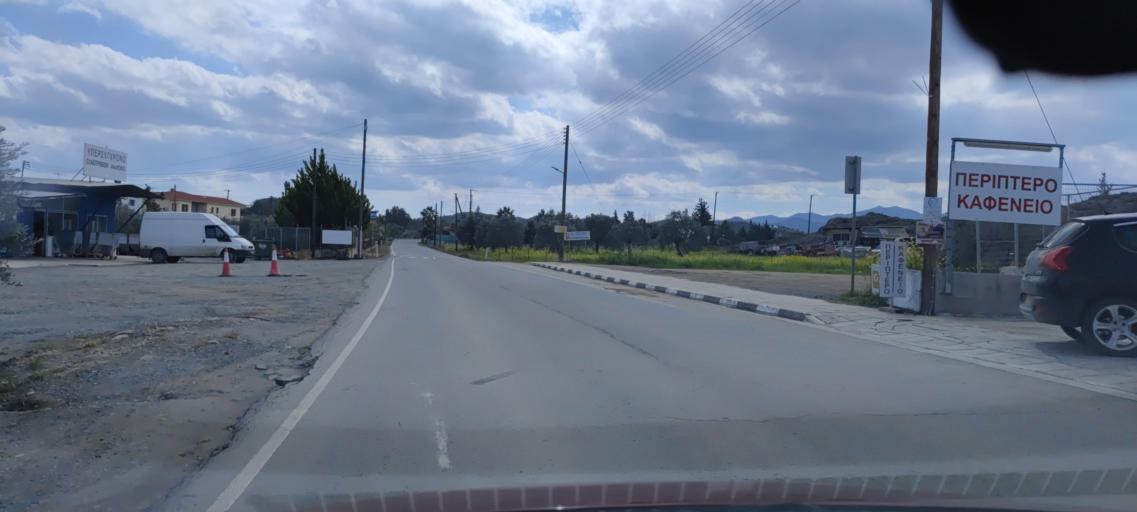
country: CY
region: Lefkosia
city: Pera
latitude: 35.0127
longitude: 33.2925
